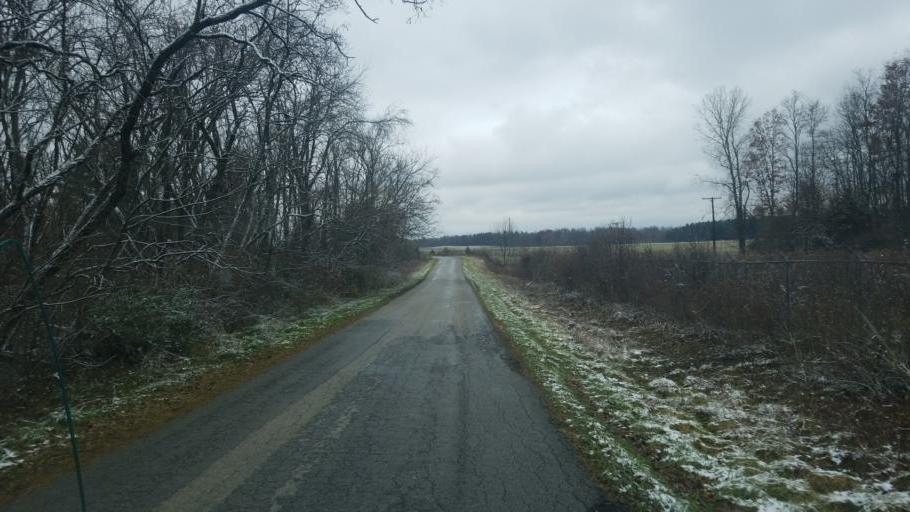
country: US
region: Ohio
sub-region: Richland County
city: Mansfield
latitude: 40.8268
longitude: -82.5269
